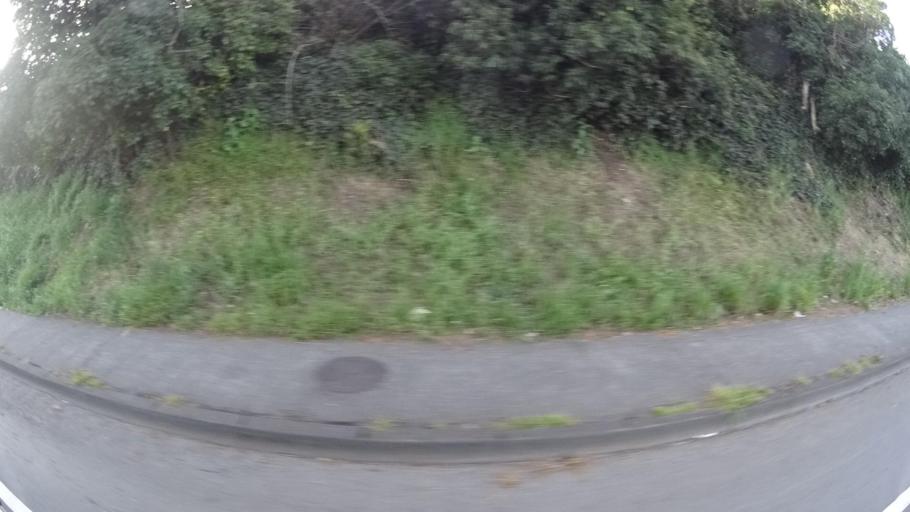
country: US
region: California
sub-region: Humboldt County
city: Bayview
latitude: 40.7799
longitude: -124.1856
